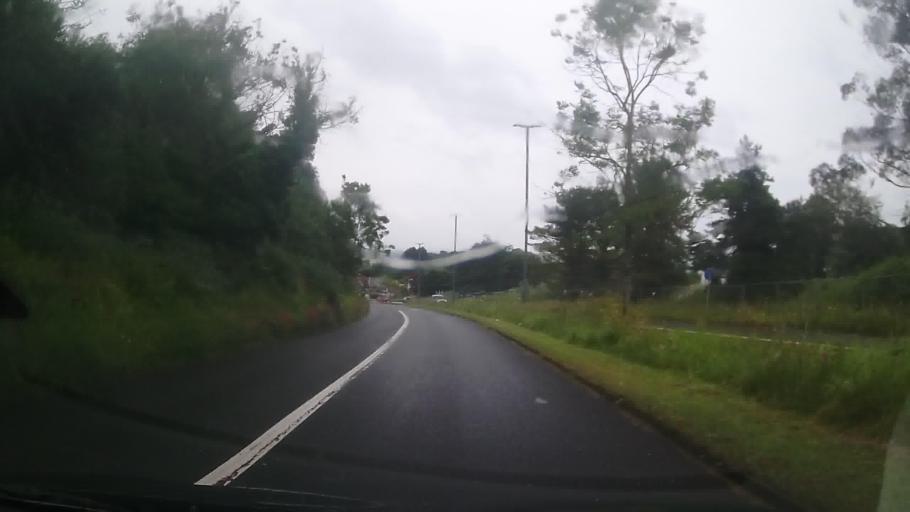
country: GB
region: England
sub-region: Borough of Torbay
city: Paignton
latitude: 50.4123
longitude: -3.5608
